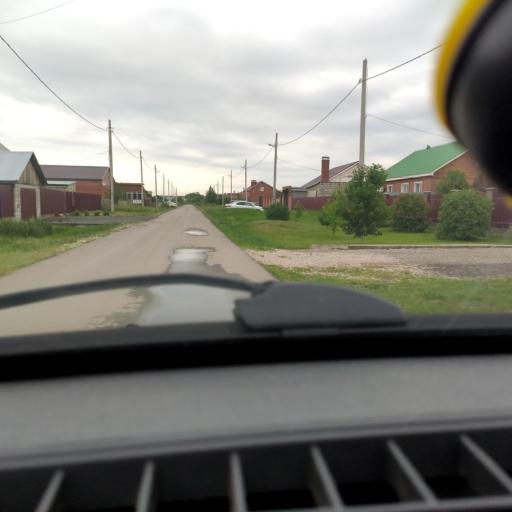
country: RU
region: Samara
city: Zhigulevsk
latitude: 53.5530
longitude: 49.5194
